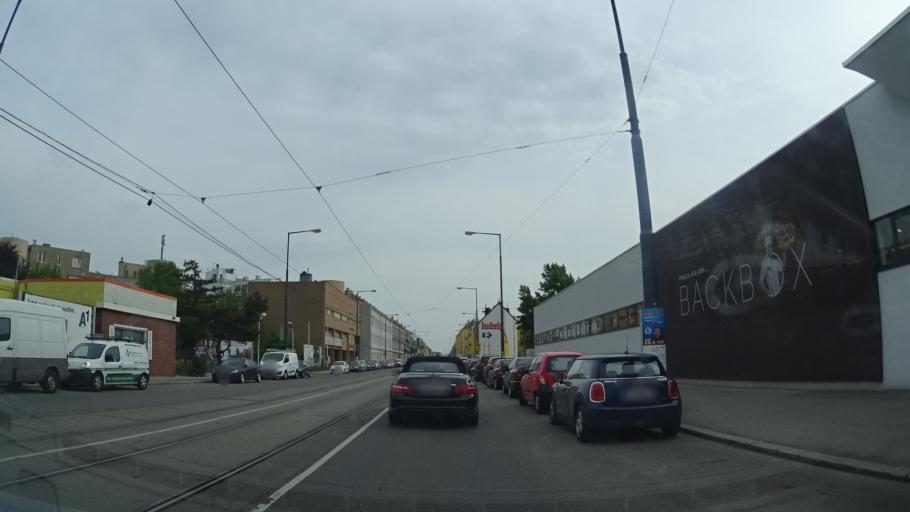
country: AT
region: Lower Austria
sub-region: Politischer Bezirk Korneuburg
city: Langenzersdorf
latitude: 48.2723
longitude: 16.3903
